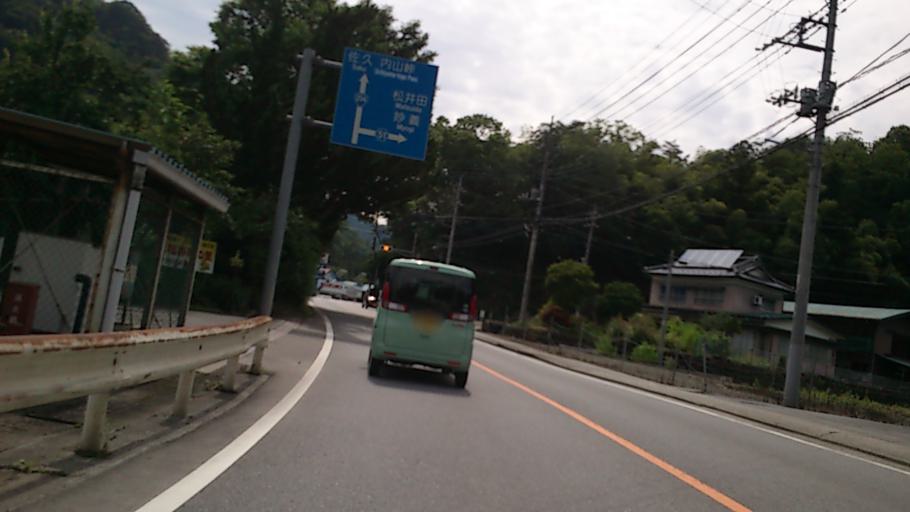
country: JP
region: Gunma
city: Tomioka
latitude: 36.2300
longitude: 138.7596
